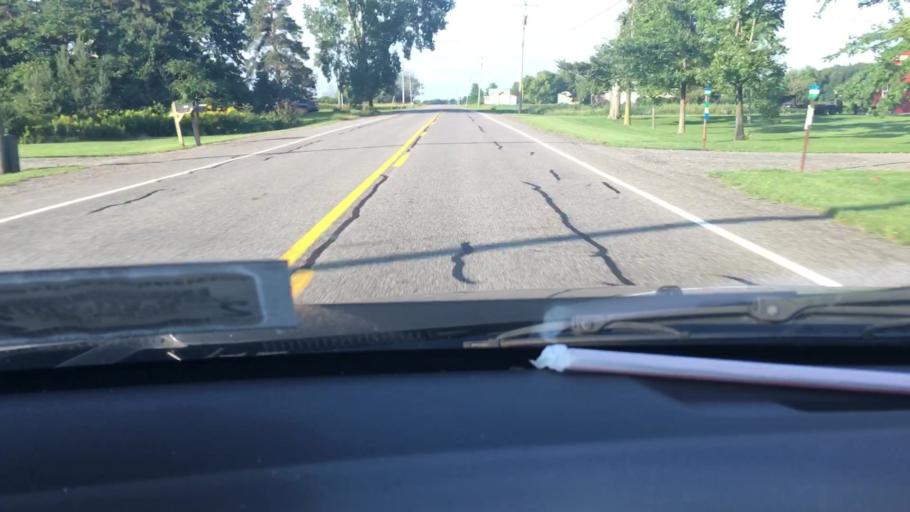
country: US
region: New York
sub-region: Genesee County
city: Batavia
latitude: 43.0369
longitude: -78.1479
